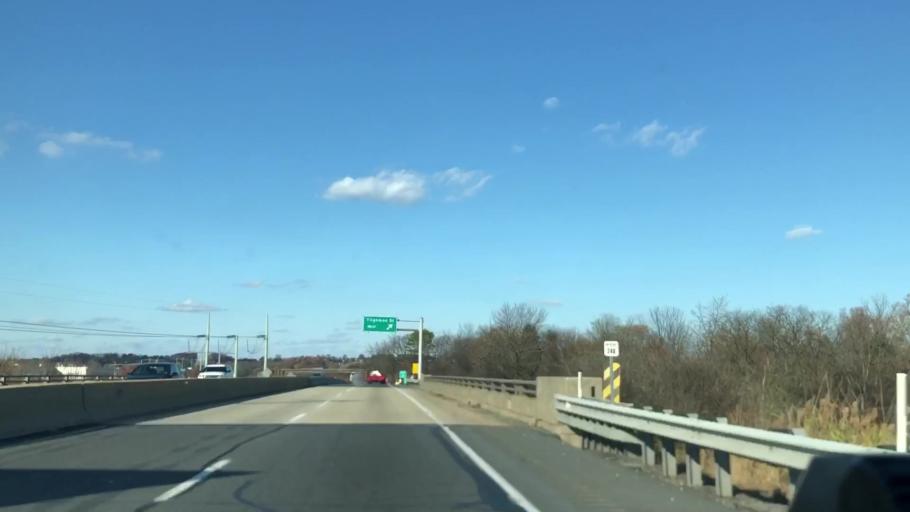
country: US
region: Pennsylvania
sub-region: Lehigh County
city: Wescosville
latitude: 40.5901
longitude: -75.5541
